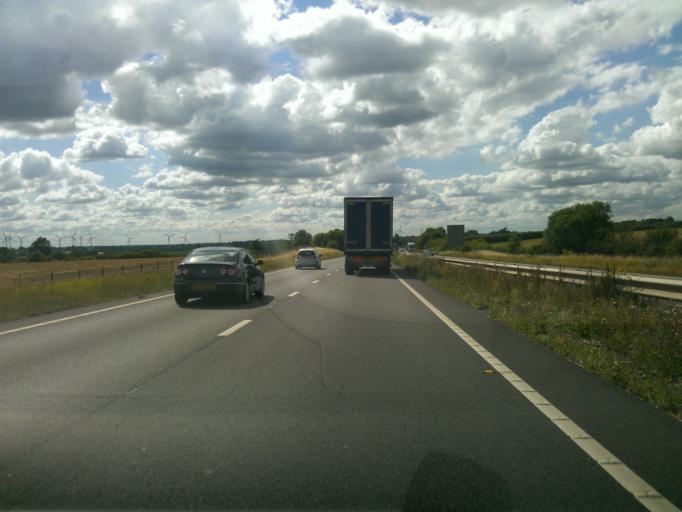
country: GB
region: England
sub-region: Northamptonshire
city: Long Buckby
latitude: 52.3923
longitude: -1.0952
